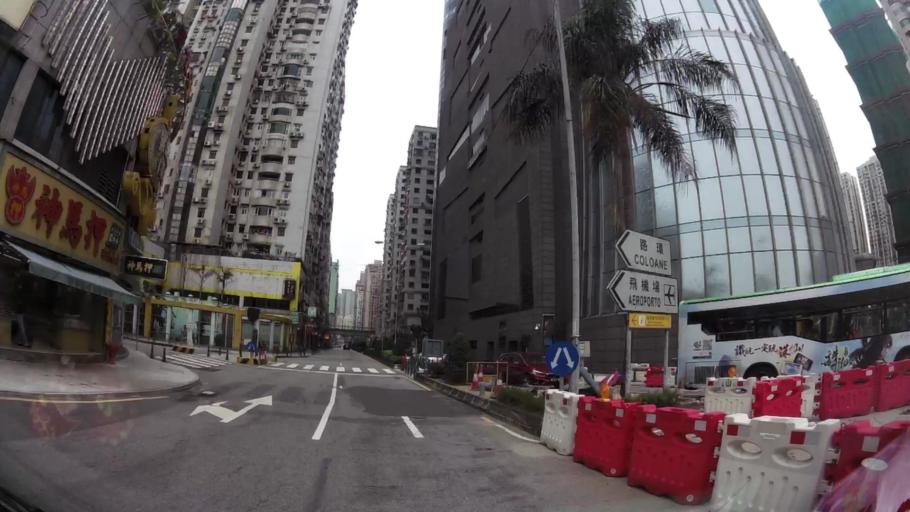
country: MO
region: Macau
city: Macau
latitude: 22.1624
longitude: 113.5551
